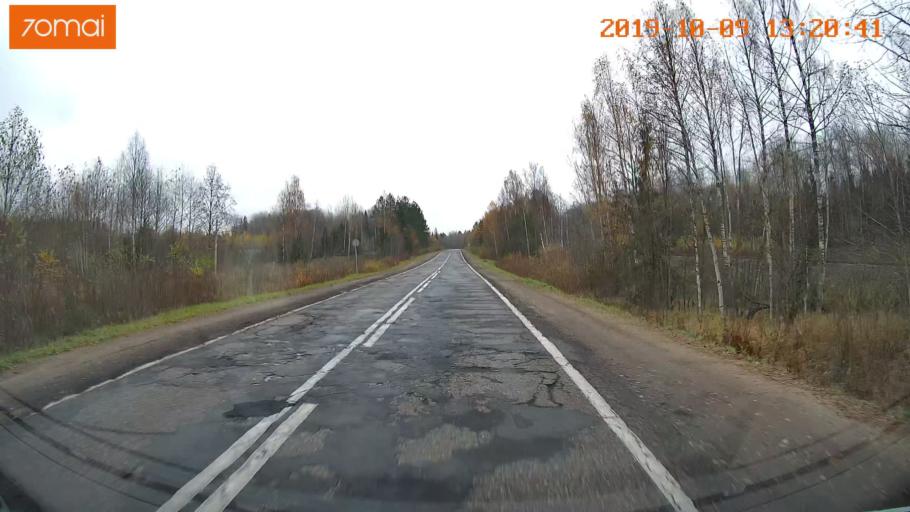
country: RU
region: Jaroslavl
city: Lyubim
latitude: 58.3421
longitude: 40.8333
